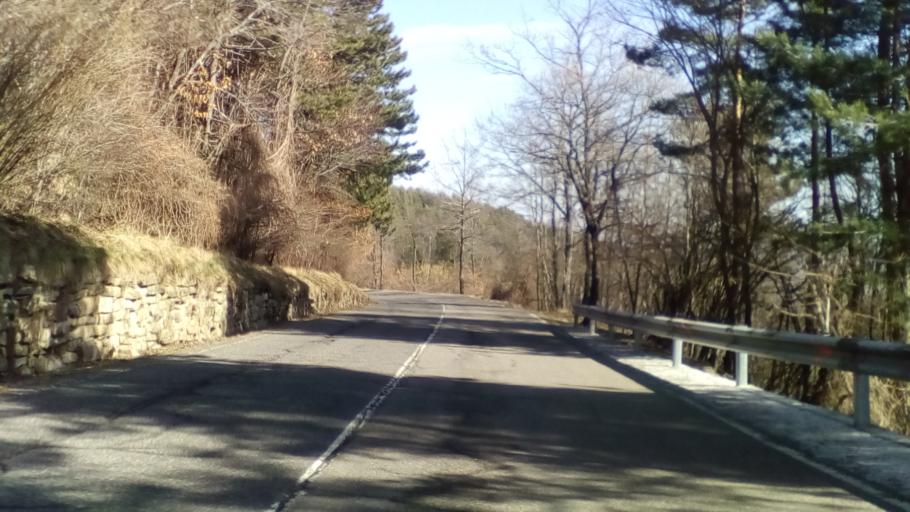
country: IT
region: Emilia-Romagna
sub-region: Provincia di Modena
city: Lama
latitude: 44.2852
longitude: 10.6997
